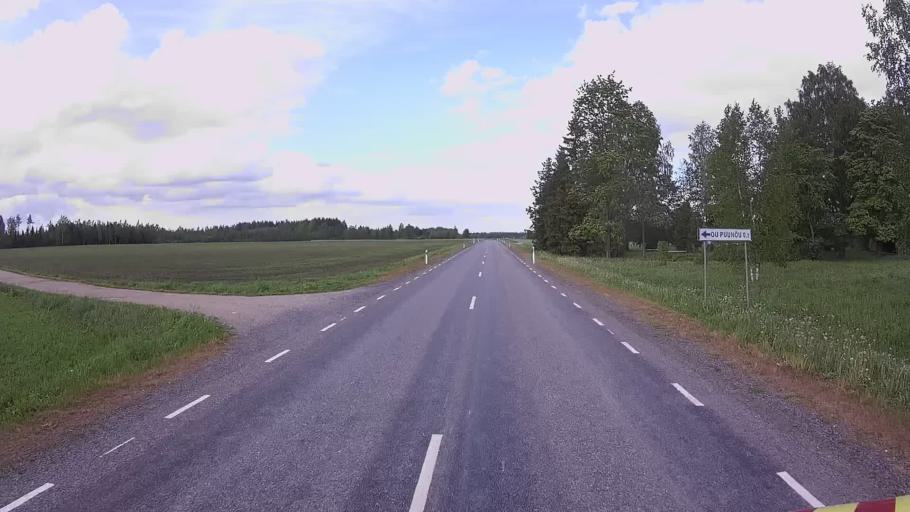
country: EE
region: Jogevamaa
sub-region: Mustvee linn
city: Mustvee
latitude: 58.9994
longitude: 26.9010
